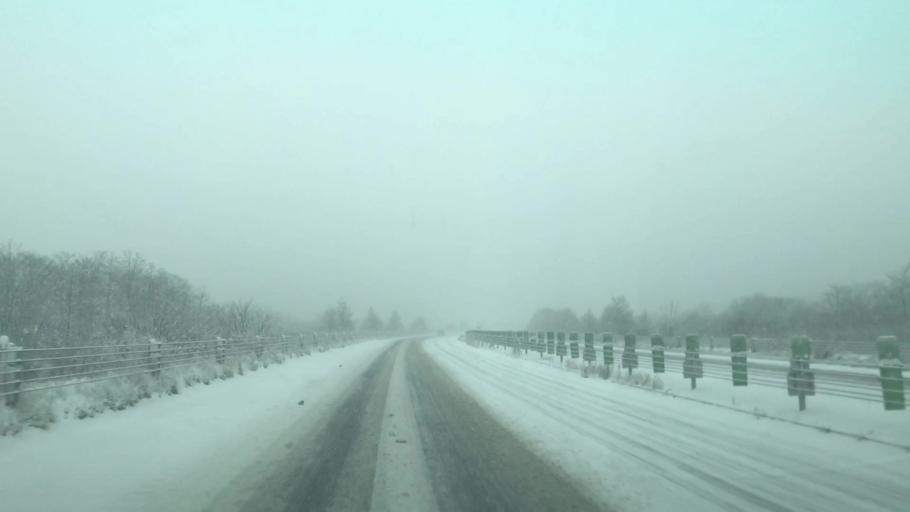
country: JP
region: Hokkaido
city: Shiraoi
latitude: 42.5068
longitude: 141.2690
